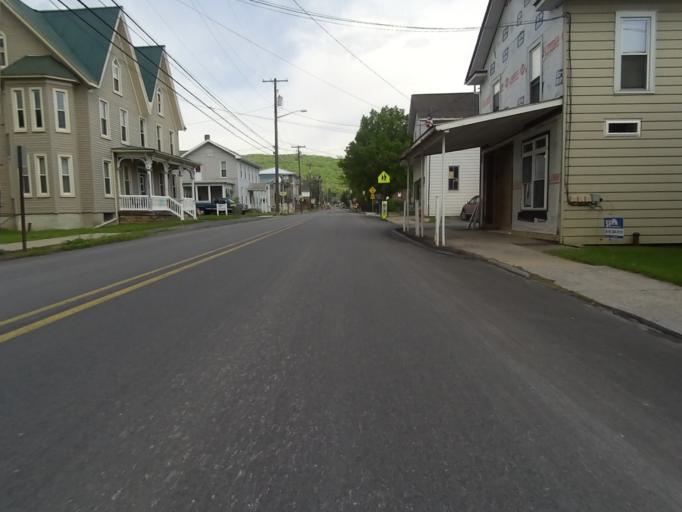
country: US
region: Pennsylvania
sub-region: Centre County
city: Zion
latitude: 41.0145
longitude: -77.6593
